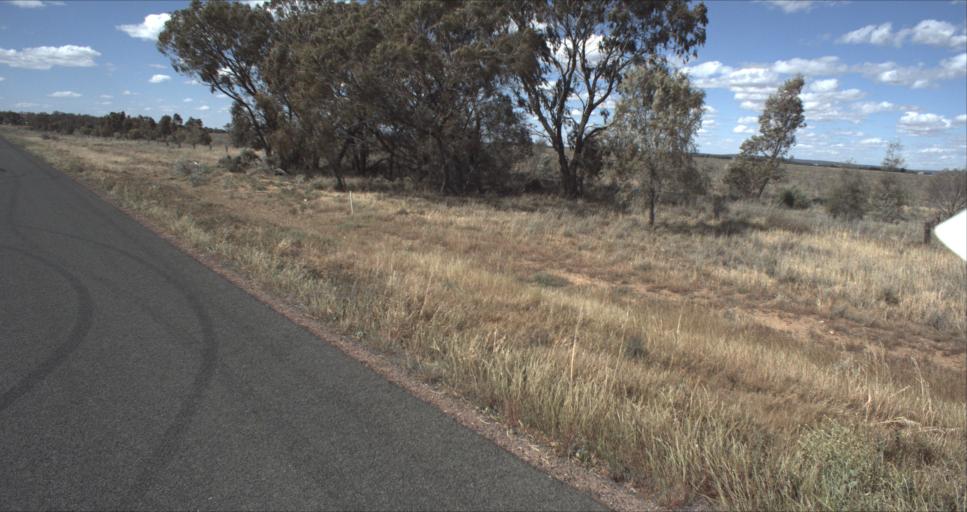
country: AU
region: New South Wales
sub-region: Leeton
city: Leeton
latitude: -34.4317
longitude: 146.2581
